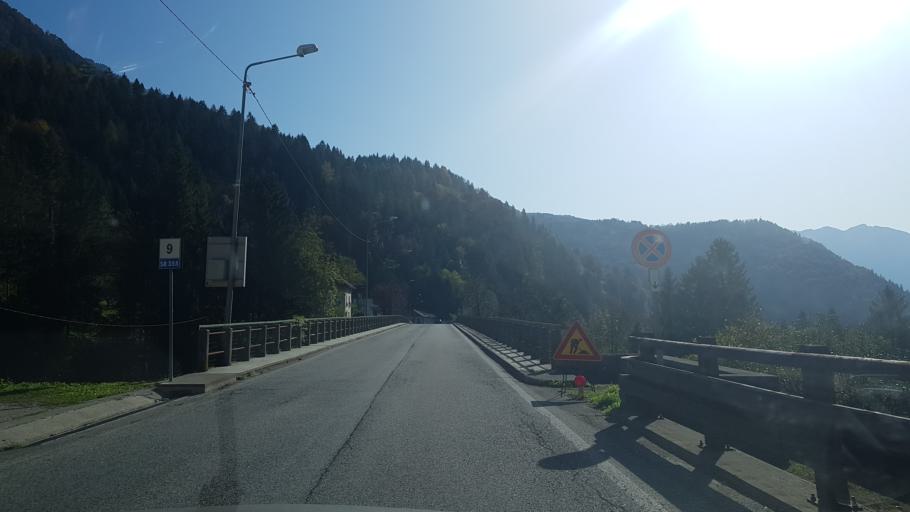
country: IT
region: Friuli Venezia Giulia
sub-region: Provincia di Udine
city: Ovaro
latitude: 46.4785
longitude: 12.8684
